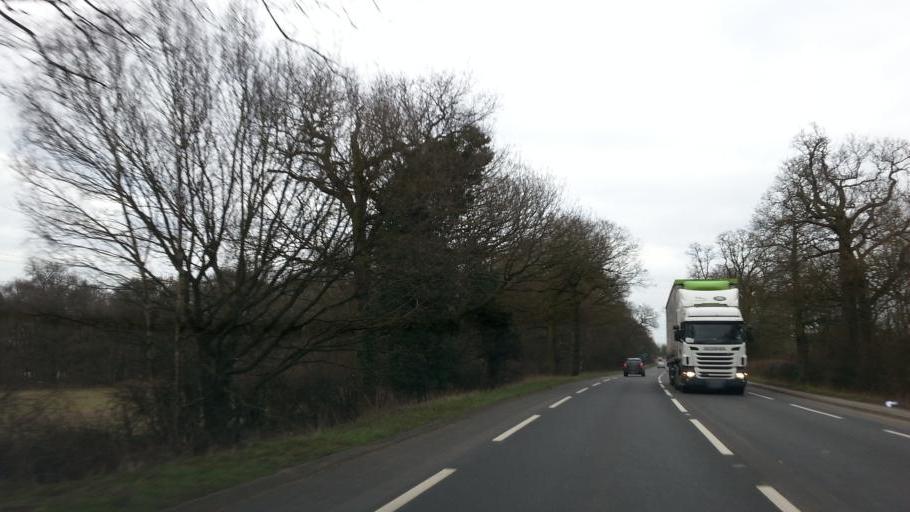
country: GB
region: England
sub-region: Solihull
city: Chelmsley Wood
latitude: 52.4700
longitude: -1.7148
